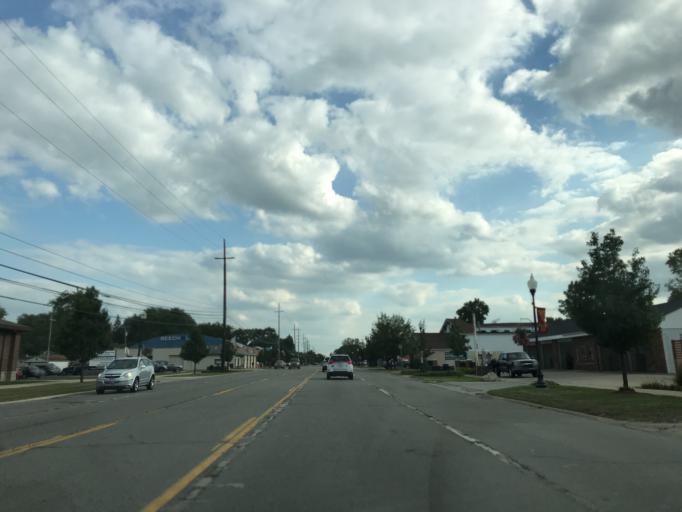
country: US
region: Michigan
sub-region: Wayne County
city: Redford
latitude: 42.4033
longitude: -83.2961
